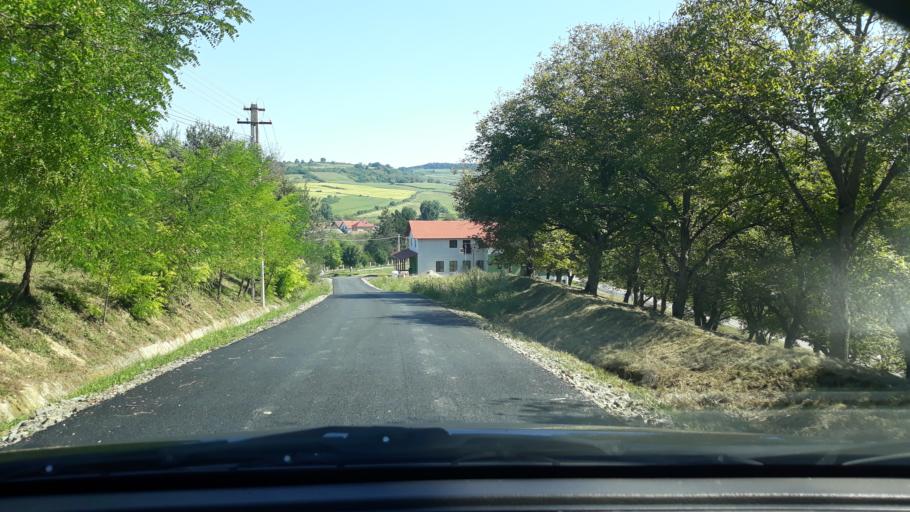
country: RO
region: Salaj
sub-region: Comuna Dobrin
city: Dobrin
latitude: 47.2905
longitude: 23.0930
